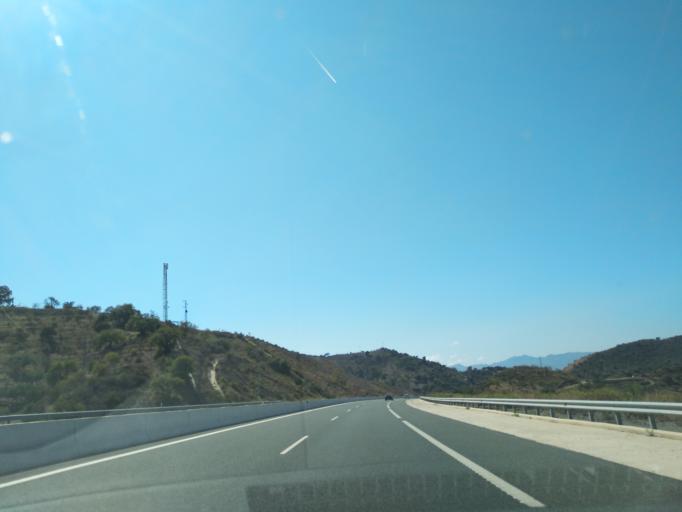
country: ES
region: Andalusia
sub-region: Provincia de Malaga
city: Almogia
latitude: 36.7938
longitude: -4.4672
